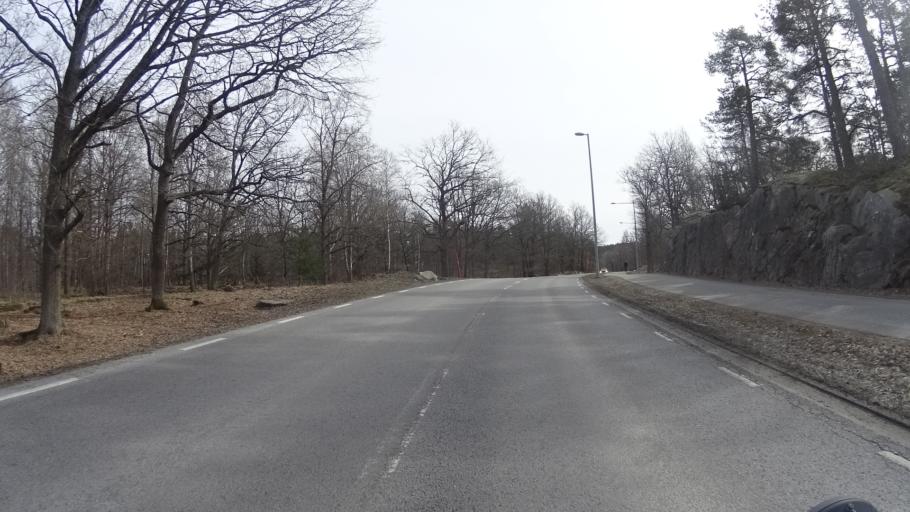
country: SE
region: Stockholm
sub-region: Nacka Kommun
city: Nacka
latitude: 59.2924
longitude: 18.1492
